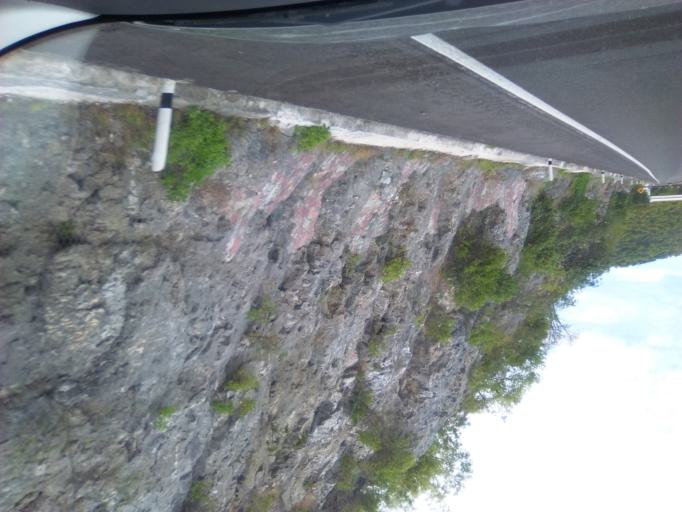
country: MX
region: Guerrero
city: Huitziltepec
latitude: 17.7077
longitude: -99.5092
